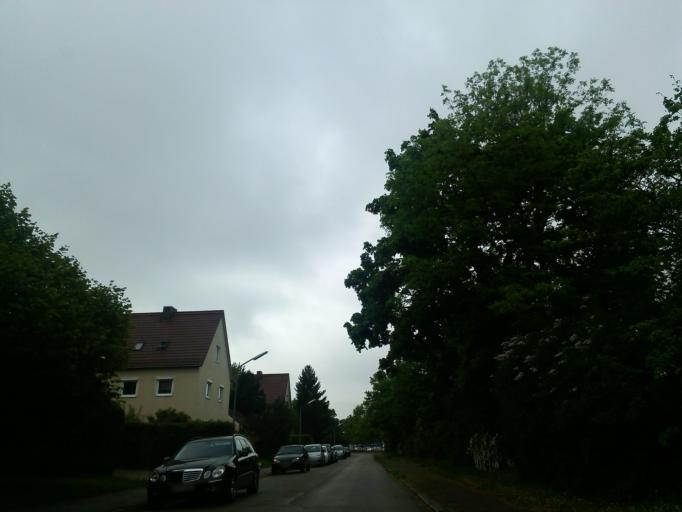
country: DE
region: Bavaria
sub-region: Upper Bavaria
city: Haar
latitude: 48.1171
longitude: 11.6857
